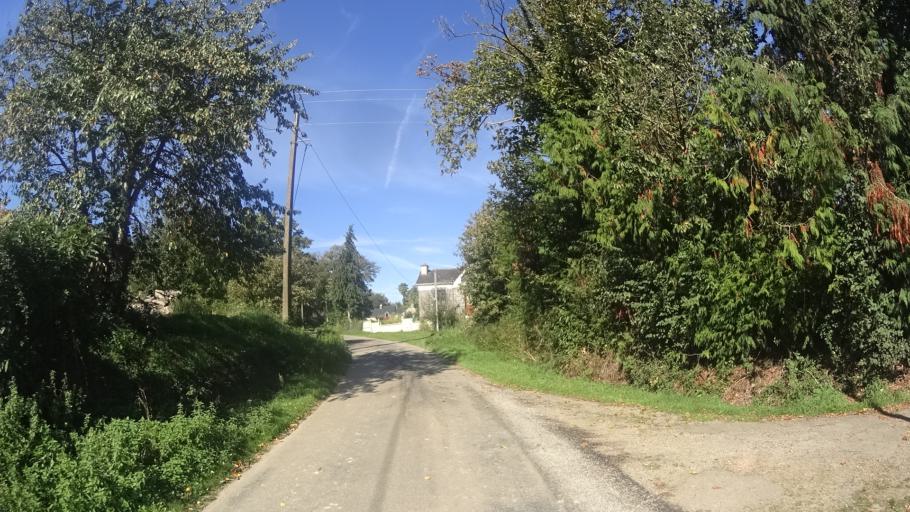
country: FR
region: Brittany
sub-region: Departement du Morbihan
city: Peillac
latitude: 47.7349
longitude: -2.1851
